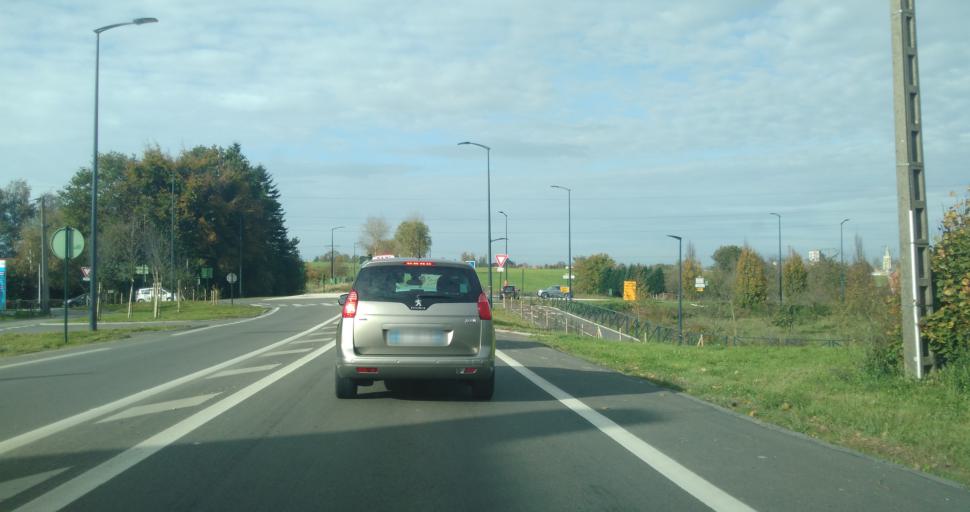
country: FR
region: Nord-Pas-de-Calais
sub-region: Departement du Pas-de-Calais
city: Aubigny-en-Artois
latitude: 50.3454
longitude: 2.5811
